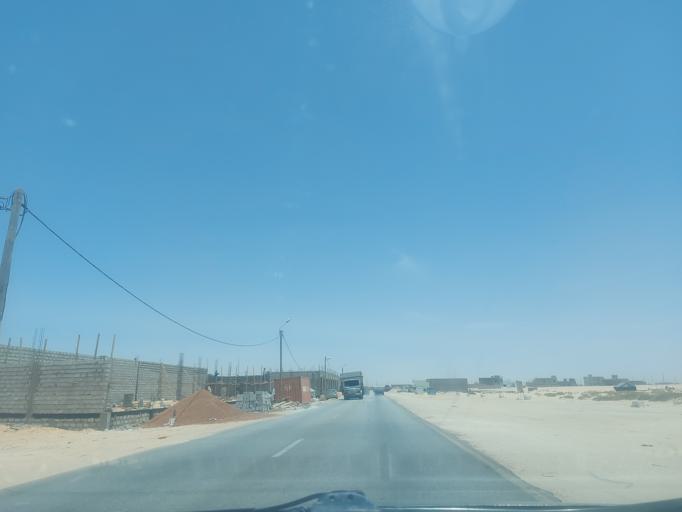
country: MR
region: Nouakchott
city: Nouakchott
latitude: 18.0832
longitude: -15.9529
